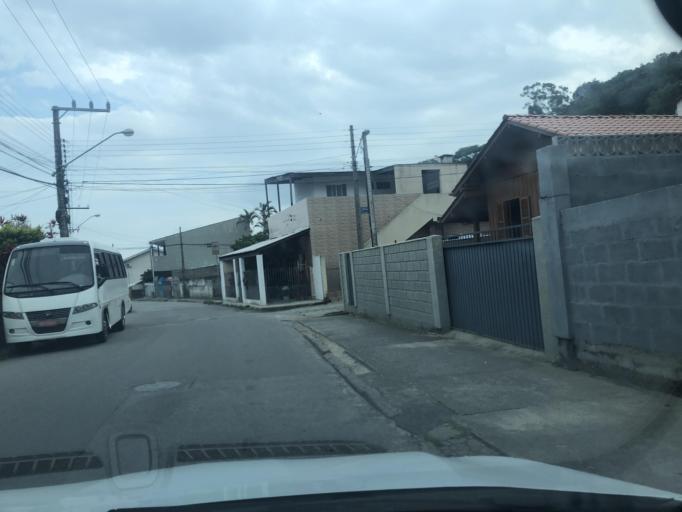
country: BR
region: Santa Catarina
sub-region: Florianopolis
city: Saco dos Limoes
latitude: -27.6026
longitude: -48.5366
